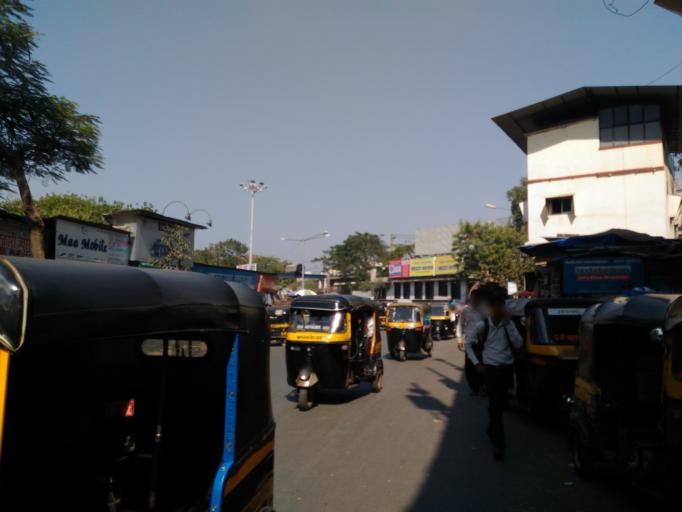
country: IN
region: Maharashtra
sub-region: Thane
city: Bhayandar
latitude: 19.3121
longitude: 72.8518
